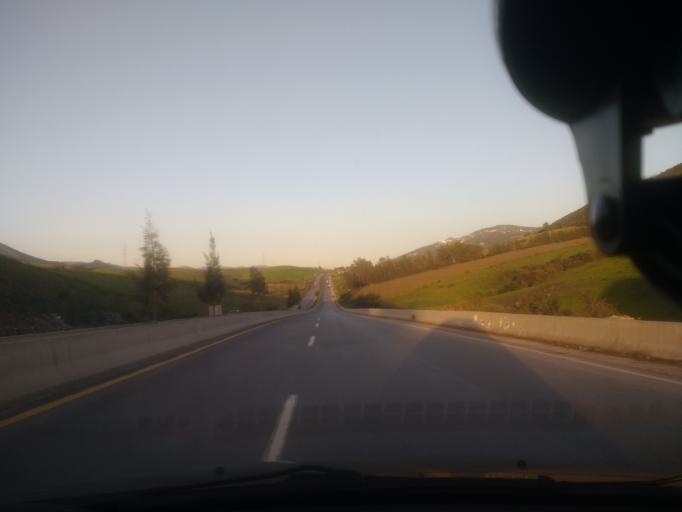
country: DZ
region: Boumerdes
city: Makouda
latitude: 36.7545
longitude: 4.0360
